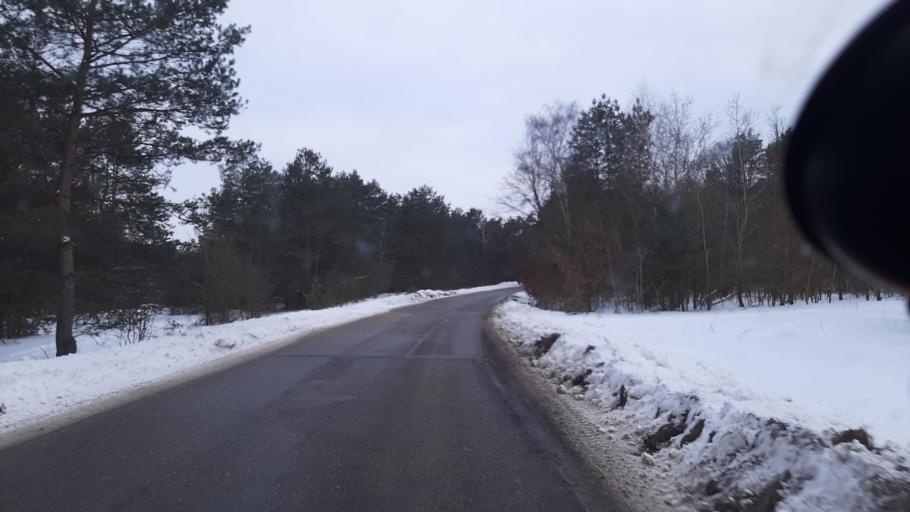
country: PL
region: Lublin Voivodeship
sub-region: Powiat lubartowski
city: Abramow
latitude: 51.4377
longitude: 22.2568
